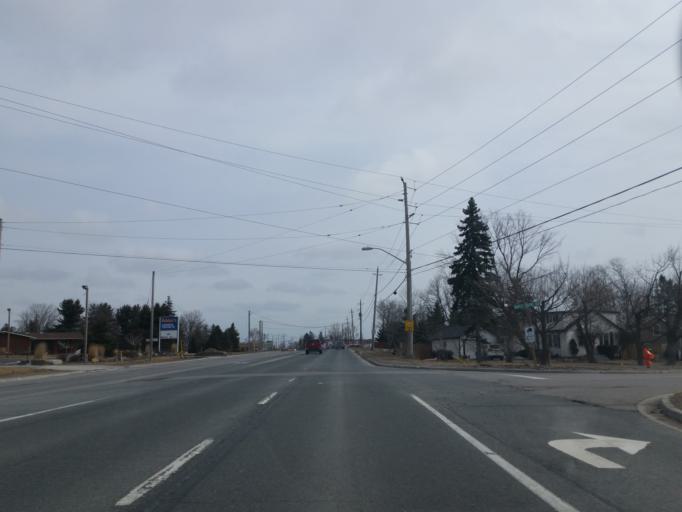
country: CA
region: Ontario
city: Oshawa
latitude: 43.9106
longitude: -78.7236
